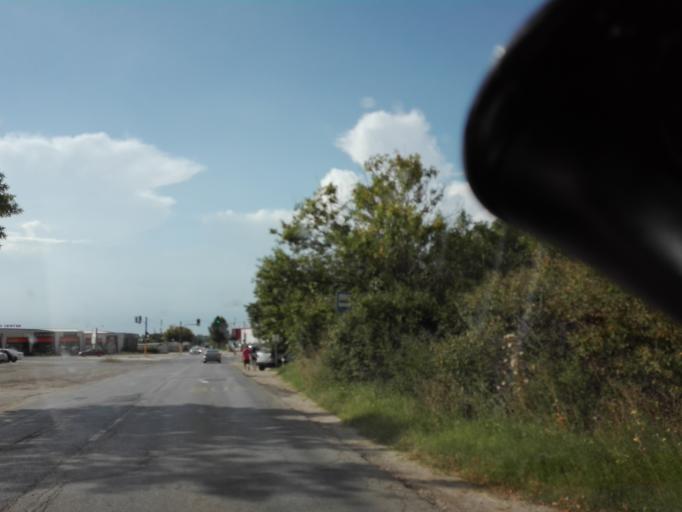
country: BG
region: Sofia-Capital
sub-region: Stolichna Obshtina
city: Sofia
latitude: 42.6258
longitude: 23.4466
